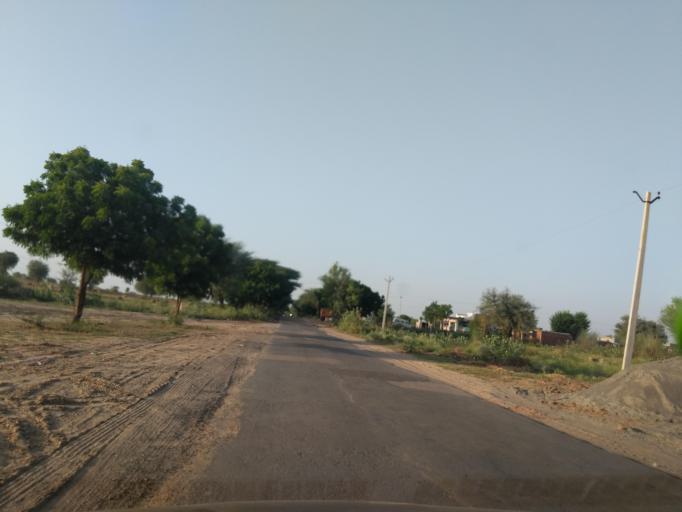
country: IN
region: Rajasthan
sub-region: Churu
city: Rajgarh
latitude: 28.5937
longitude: 75.3754
